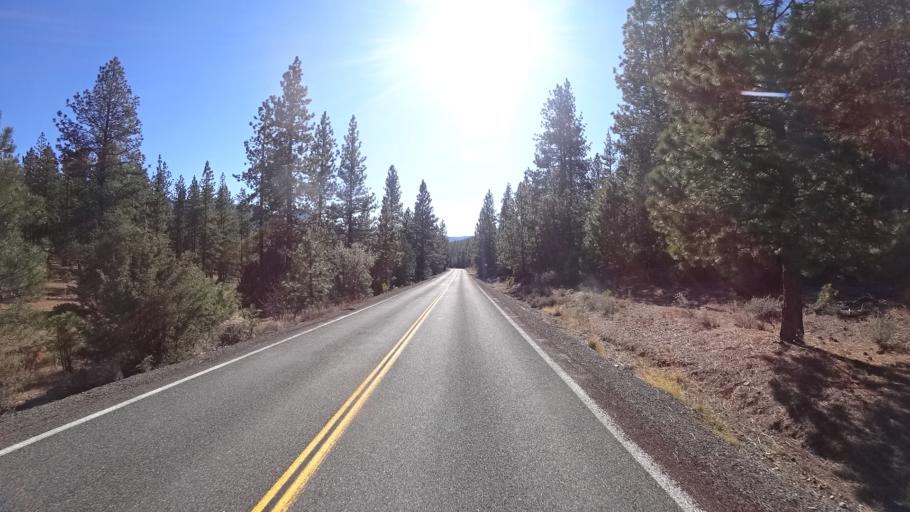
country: US
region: California
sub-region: Siskiyou County
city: Weed
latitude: 41.4341
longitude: -122.6391
